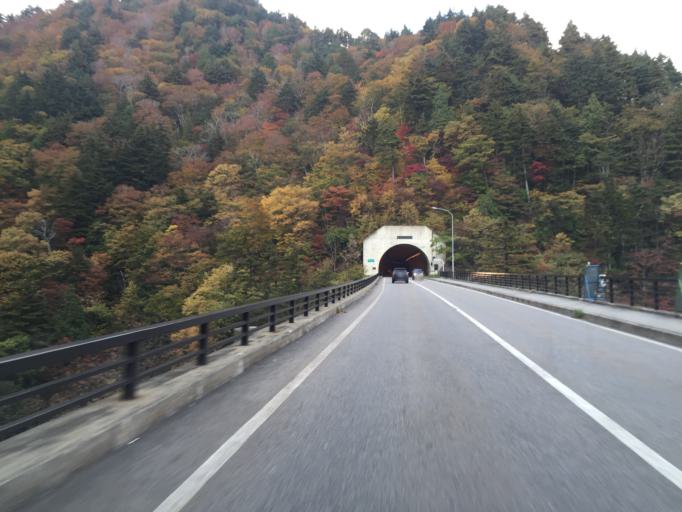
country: JP
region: Fukushima
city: Kitakata
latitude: 37.7766
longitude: 139.9228
